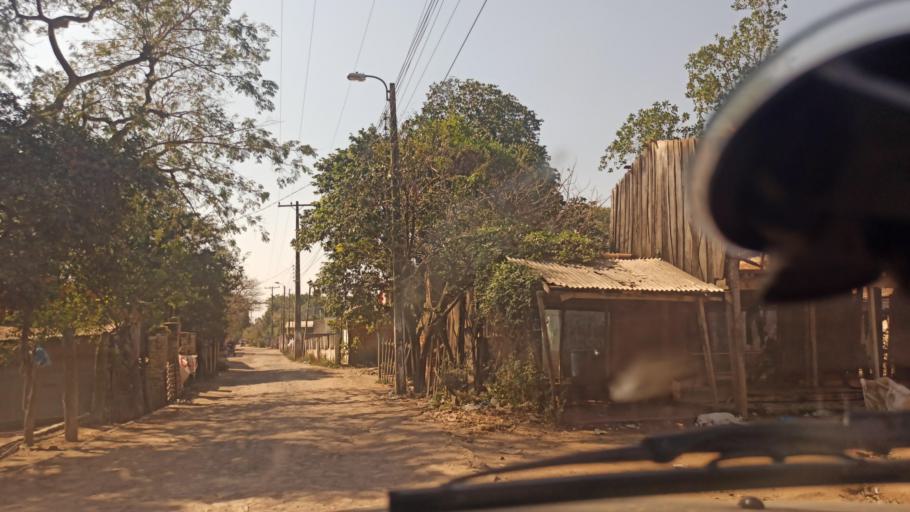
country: AR
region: Formosa
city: Clorinda
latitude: -25.2933
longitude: -57.6974
